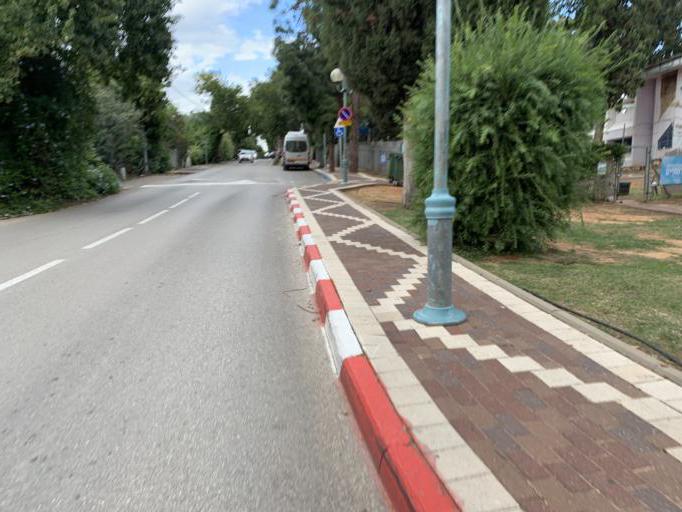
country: IL
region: Central District
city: Hod HaSharon
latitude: 32.1563
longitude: 34.8870
